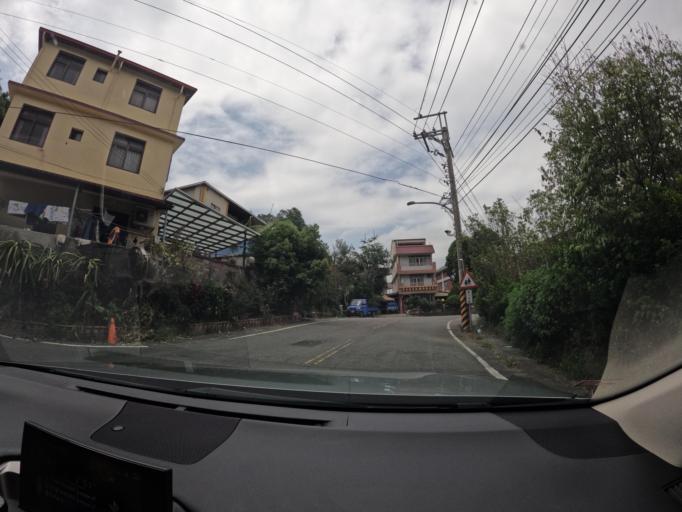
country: TW
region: Taiwan
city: Fengyuan
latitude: 24.3339
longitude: 120.8748
